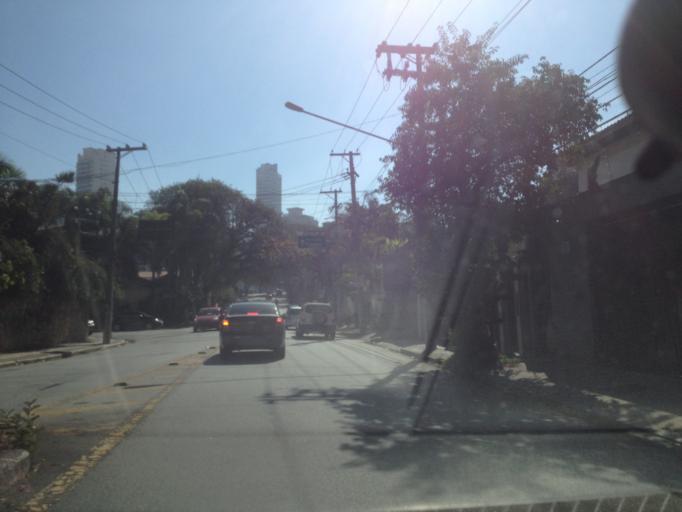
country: BR
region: Sao Paulo
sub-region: Sao Paulo
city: Sao Paulo
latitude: -23.5502
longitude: -46.6862
